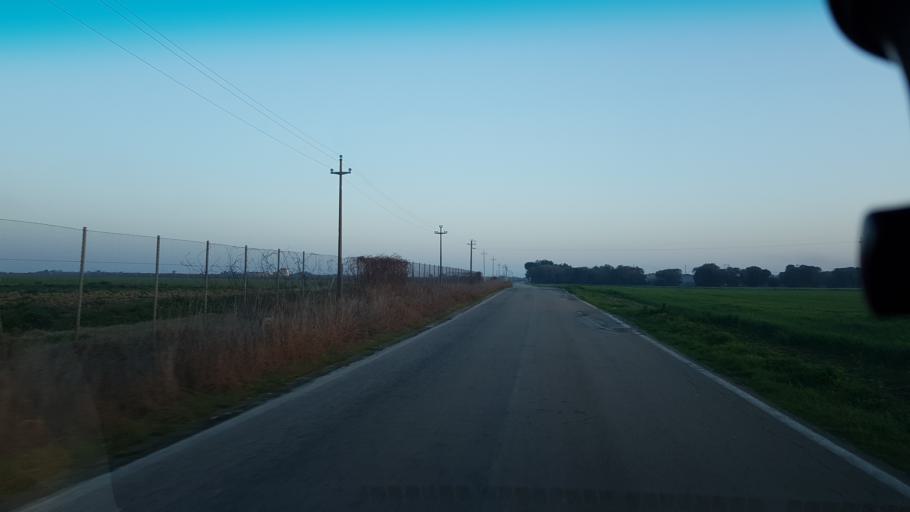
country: IT
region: Apulia
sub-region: Provincia di Brindisi
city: Mesagne
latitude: 40.5978
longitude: 17.7941
